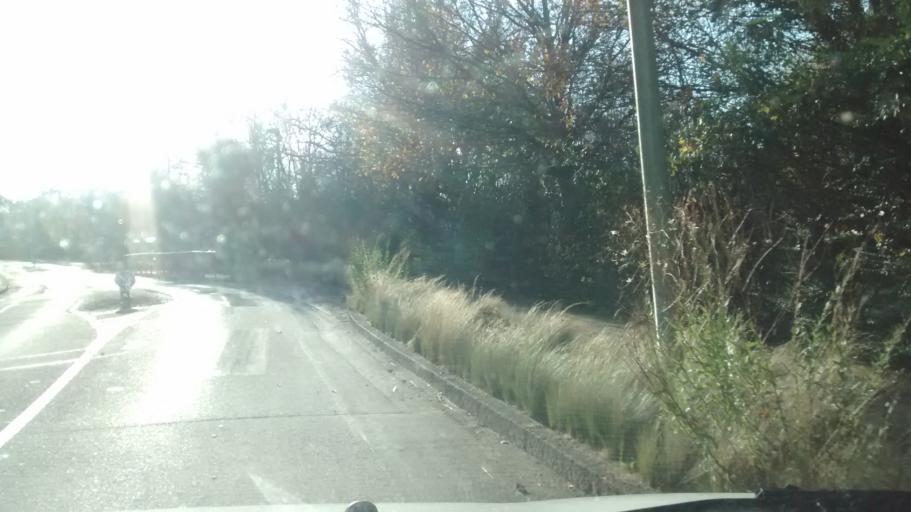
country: FR
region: Brittany
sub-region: Departement d'Ille-et-Vilaine
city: Pace
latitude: 48.1534
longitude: -1.7833
